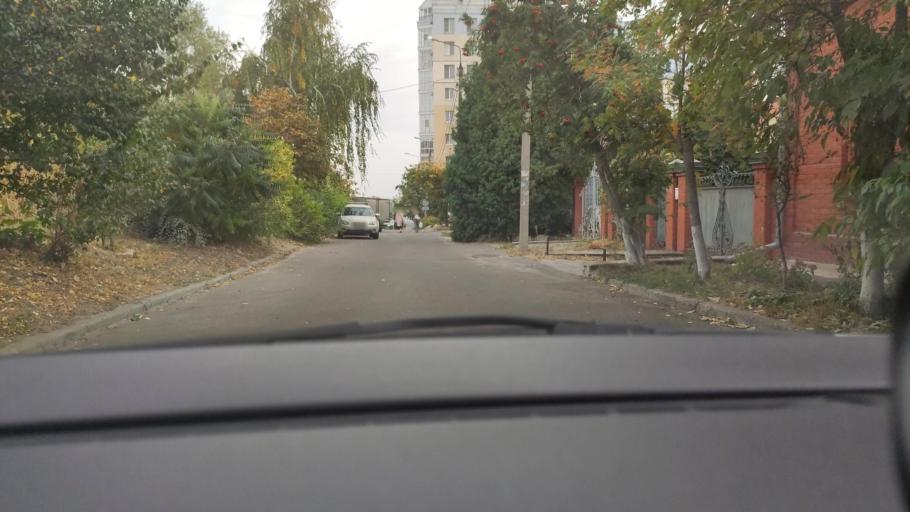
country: RU
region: Voronezj
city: Voronezh
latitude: 51.6634
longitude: 39.2162
